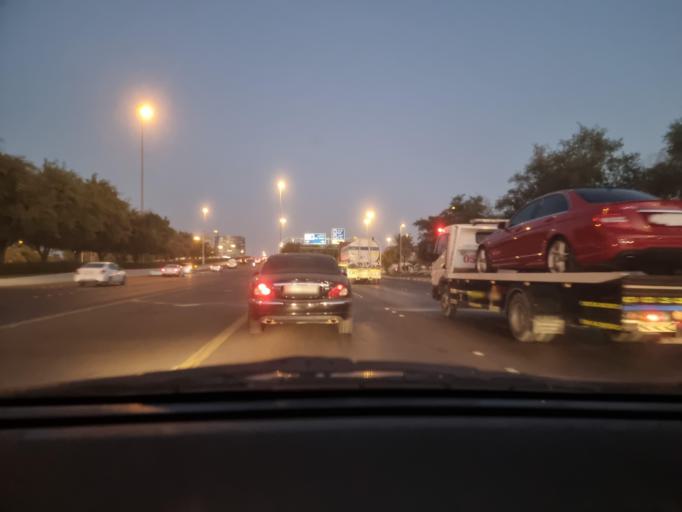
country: AE
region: Abu Dhabi
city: Abu Dhabi
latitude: 24.3741
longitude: 54.5201
